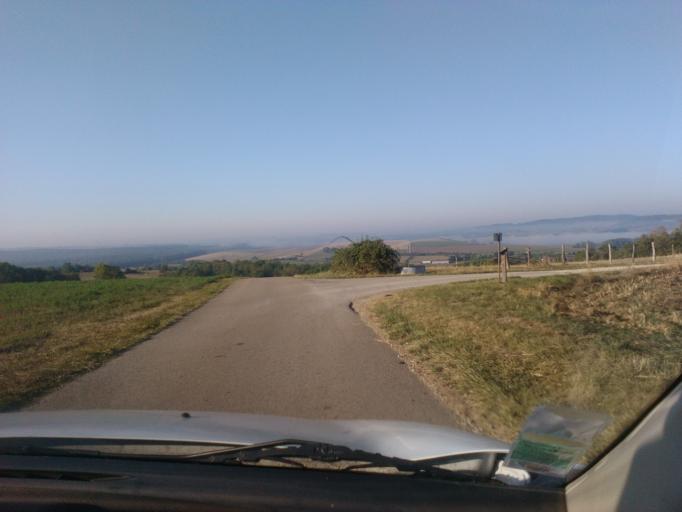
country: FR
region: Lorraine
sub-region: Departement des Vosges
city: Mirecourt
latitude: 48.2685
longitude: 6.1843
